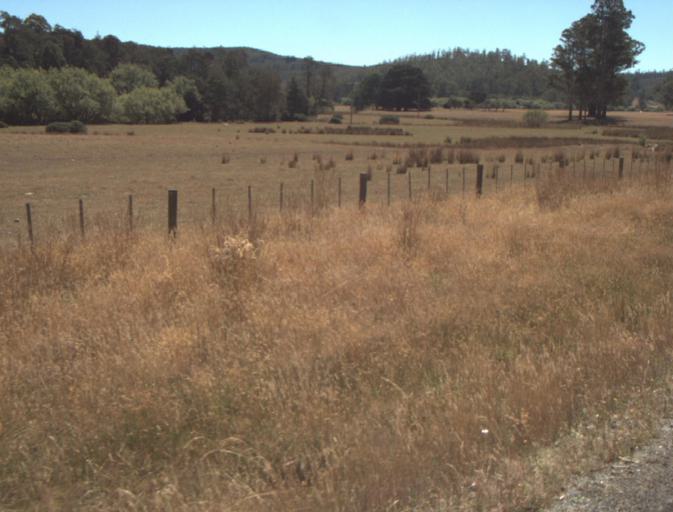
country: AU
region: Tasmania
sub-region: Dorset
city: Scottsdale
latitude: -41.2968
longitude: 147.3849
